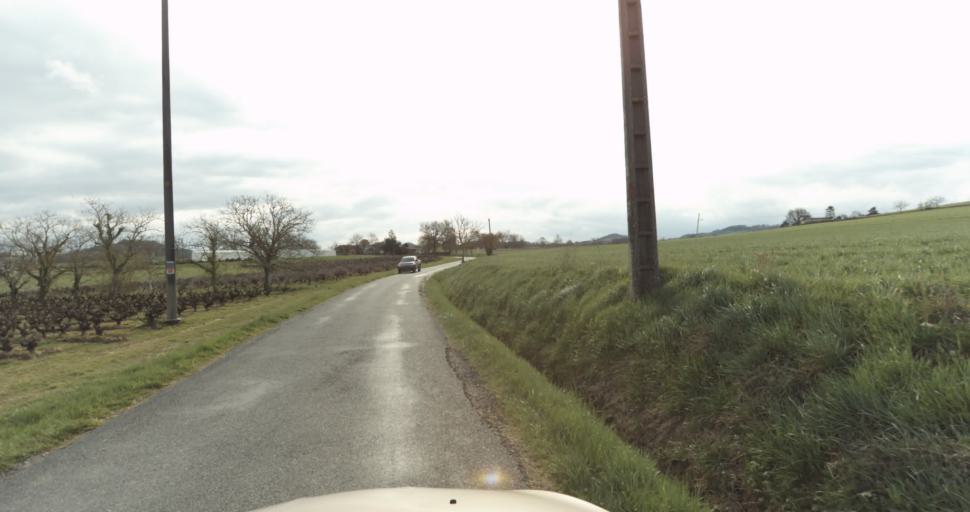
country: FR
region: Midi-Pyrenees
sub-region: Departement du Tarn
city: Puygouzon
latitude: 43.8891
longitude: 2.1900
